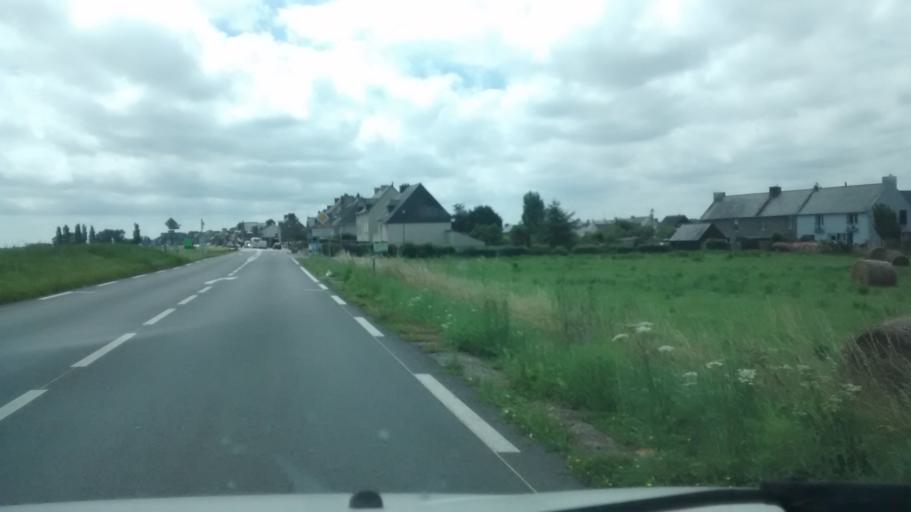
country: FR
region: Brittany
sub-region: Departement d'Ille-et-Vilaine
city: La Fresnais
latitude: 48.6252
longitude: -1.8582
